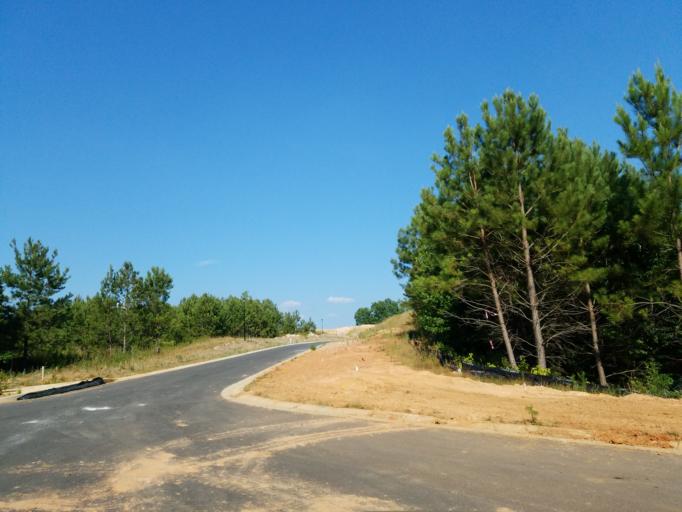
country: US
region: Georgia
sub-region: Fulton County
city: Milton
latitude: 34.1811
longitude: -84.3329
